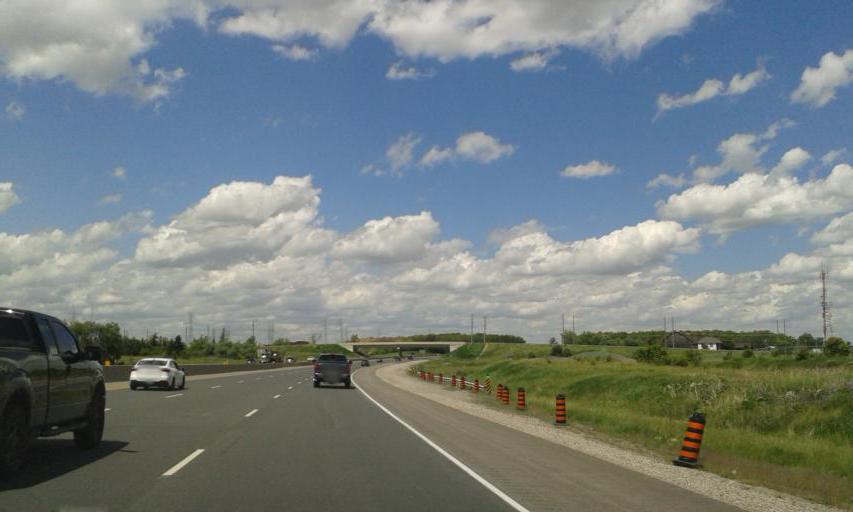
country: CA
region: Ontario
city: Oakville
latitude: 43.4955
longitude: -79.7594
